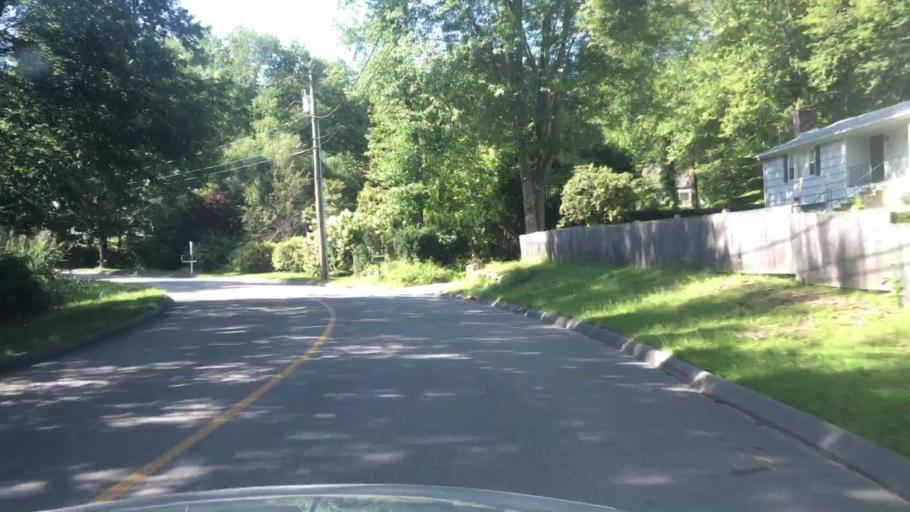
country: US
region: Connecticut
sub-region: Middlesex County
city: Deep River Center
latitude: 41.3677
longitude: -72.4439
